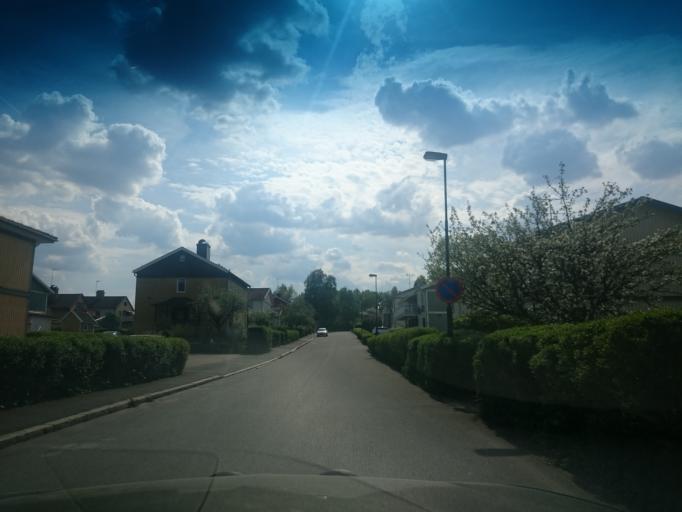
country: SE
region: Joenkoeping
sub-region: Vetlanda Kommun
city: Vetlanda
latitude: 57.4330
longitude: 15.0707
